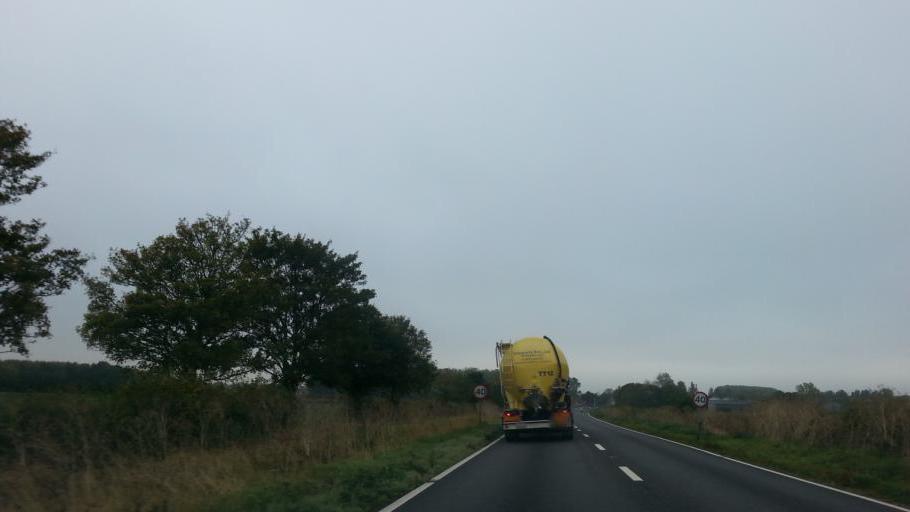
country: GB
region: England
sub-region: Northamptonshire
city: Thrapston
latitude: 52.4260
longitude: -0.4898
